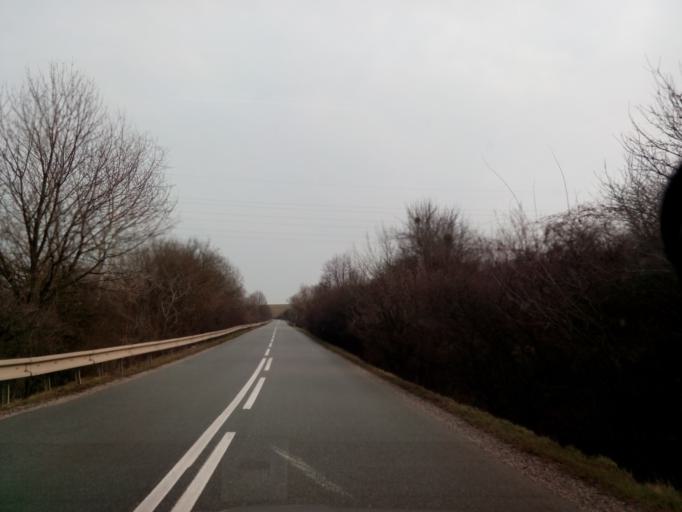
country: SK
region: Kosicky
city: Secovce
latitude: 48.6240
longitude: 21.5492
